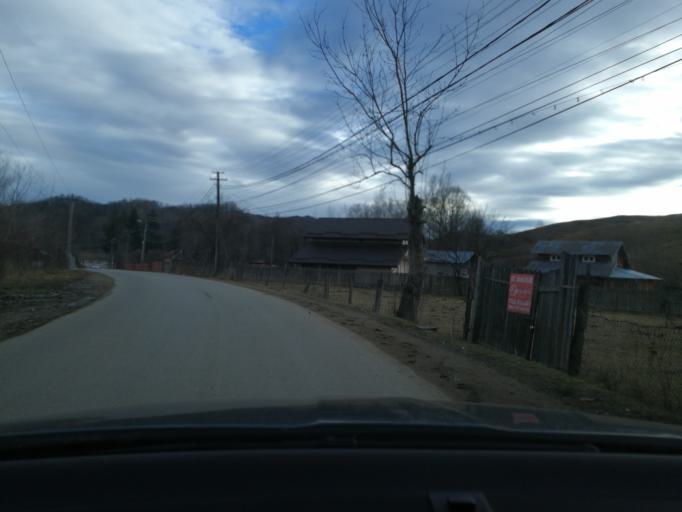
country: RO
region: Prahova
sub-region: Oras Breaza
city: Valea Tarsei
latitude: 45.1831
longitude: 25.6315
